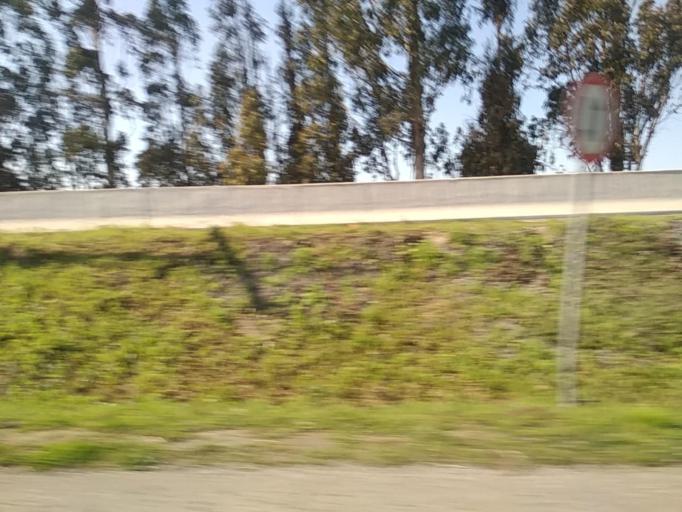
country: CL
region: Valparaiso
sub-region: Provincia de Marga Marga
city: Villa Alemana
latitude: -33.3419
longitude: -71.3615
